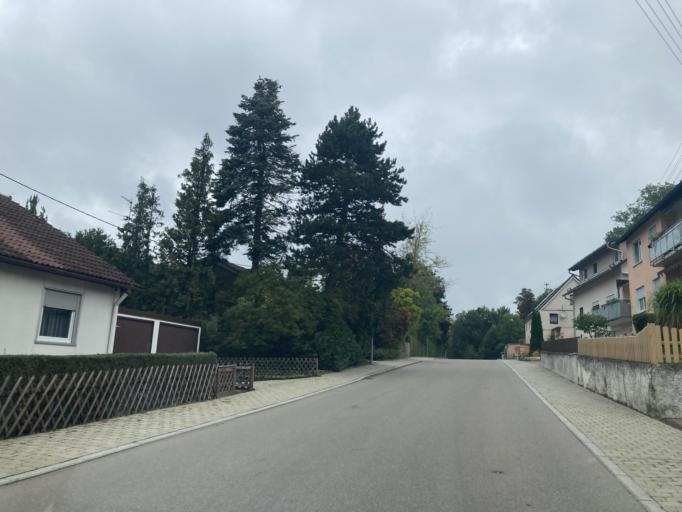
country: DE
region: Baden-Wuerttemberg
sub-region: Regierungsbezirk Stuttgart
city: Dischingen
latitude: 48.6928
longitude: 10.3648
